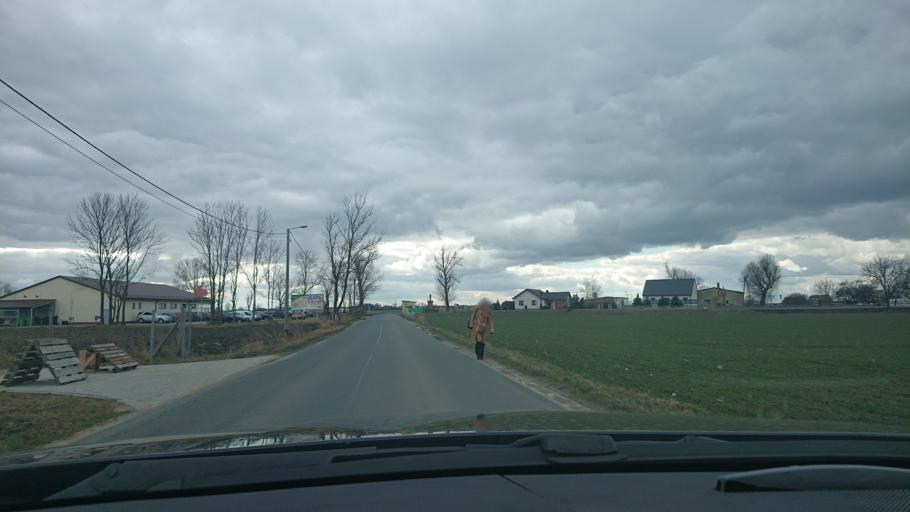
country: PL
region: Greater Poland Voivodeship
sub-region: Powiat gnieznienski
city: Gniezno
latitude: 52.5718
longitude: 17.6141
